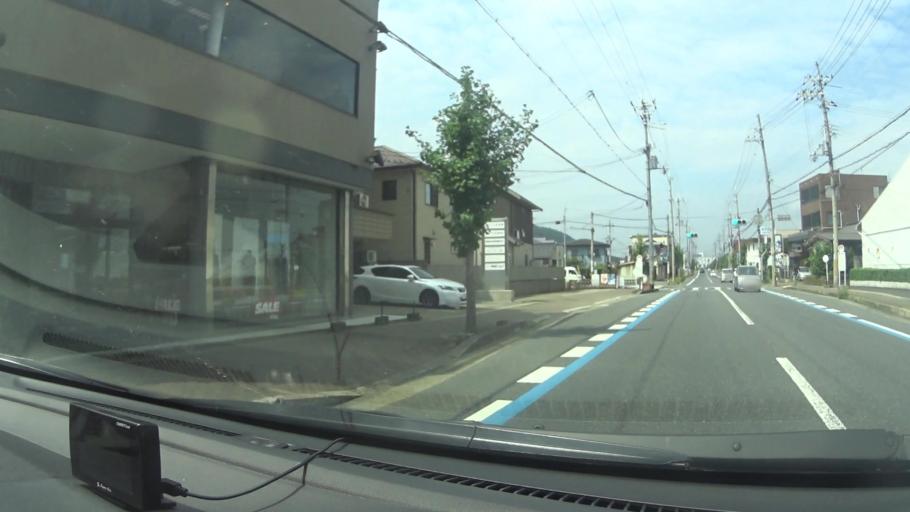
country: JP
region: Kyoto
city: Ayabe
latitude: 35.3023
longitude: 135.2382
